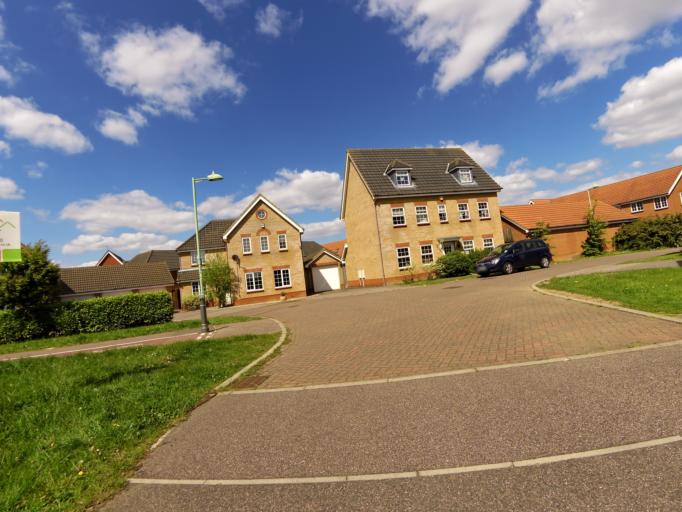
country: GB
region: England
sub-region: Suffolk
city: Kessingland
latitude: 52.4483
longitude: 1.7078
